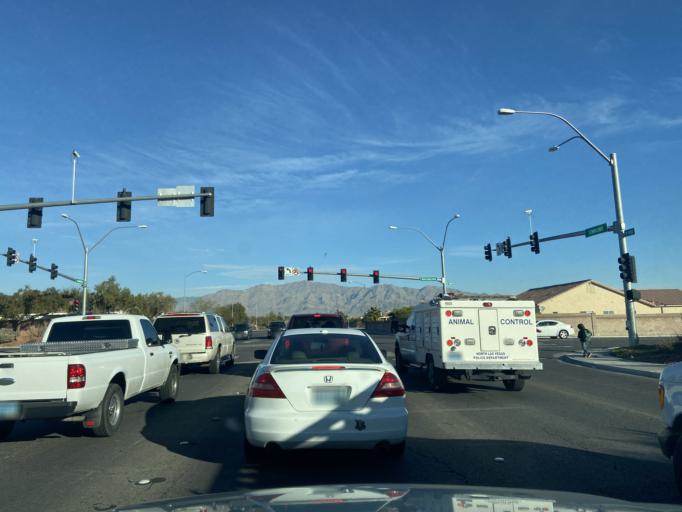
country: US
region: Nevada
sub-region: Clark County
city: North Las Vegas
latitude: 36.2538
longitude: -115.1800
